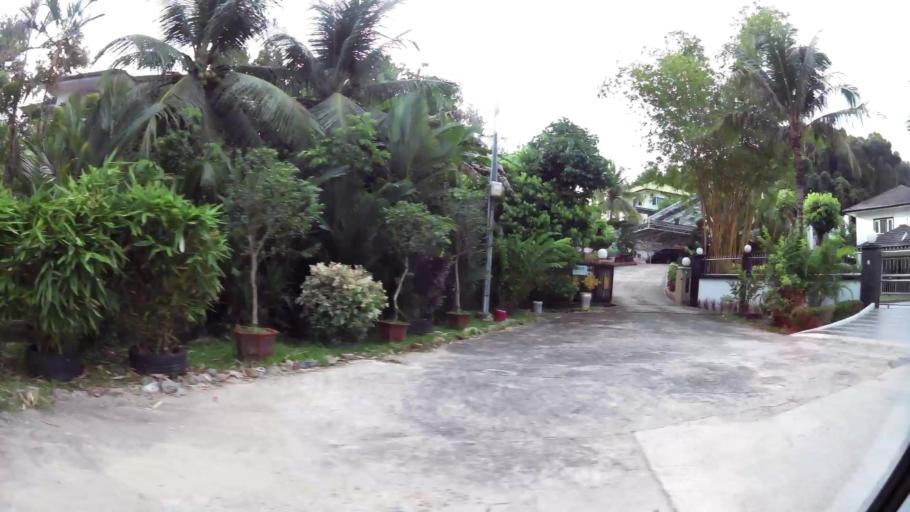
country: BN
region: Brunei and Muara
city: Bandar Seri Begawan
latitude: 4.9520
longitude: 114.9800
